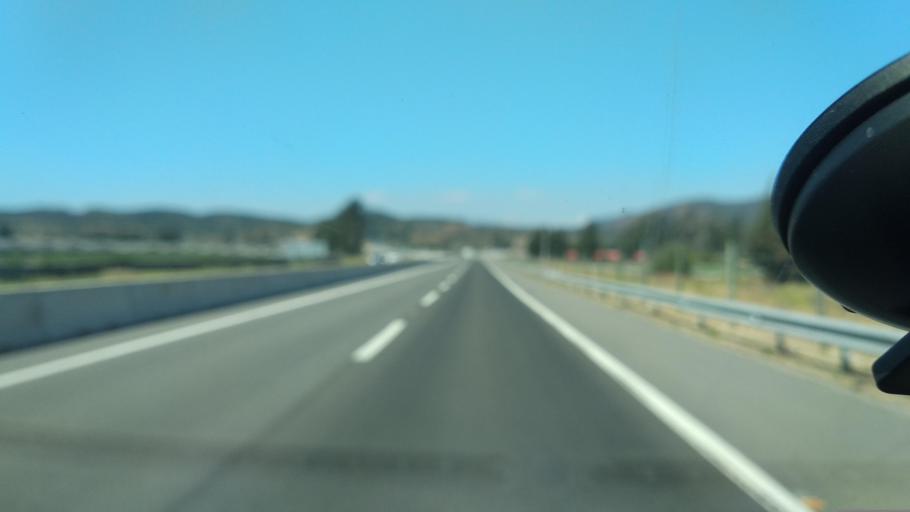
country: CL
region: Valparaiso
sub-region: Provincia de Marga Marga
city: Limache
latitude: -32.9800
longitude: -71.3074
